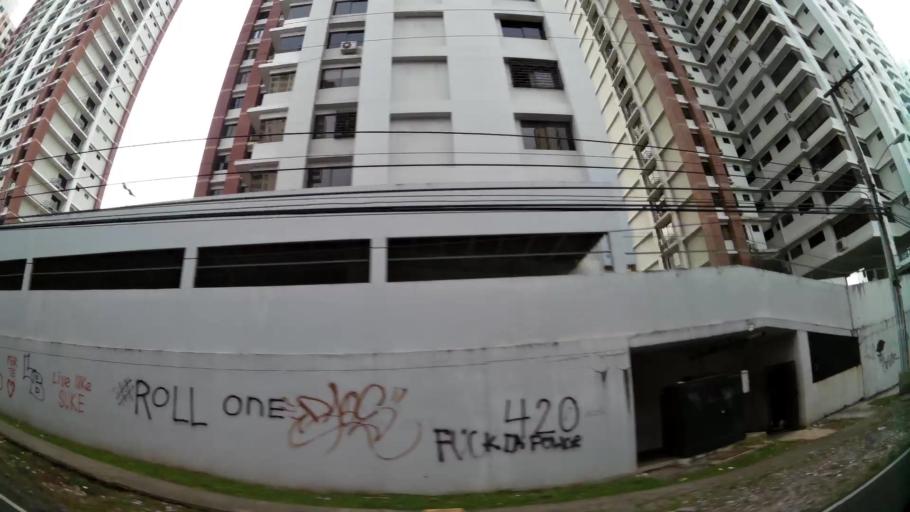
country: PA
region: Panama
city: Panama
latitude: 8.9894
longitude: -79.5060
